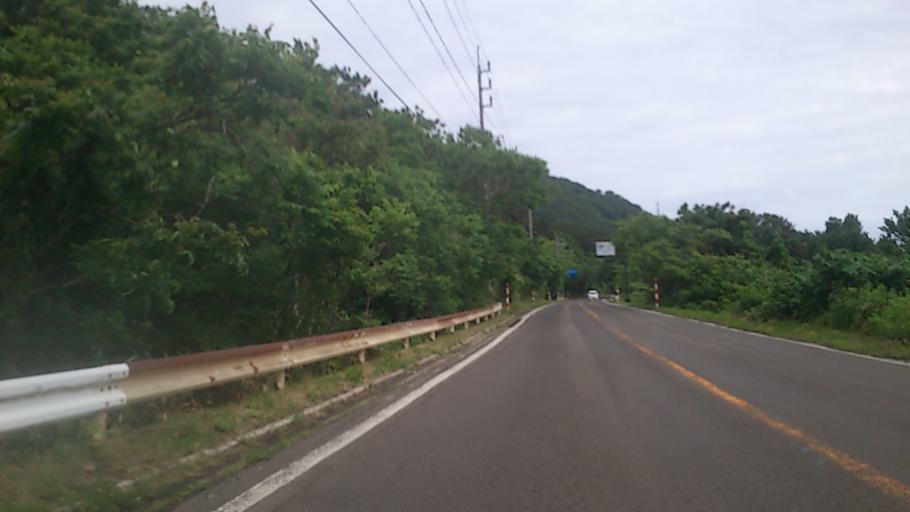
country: JP
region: Akita
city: Noshiromachi
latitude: 40.4253
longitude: 139.9444
